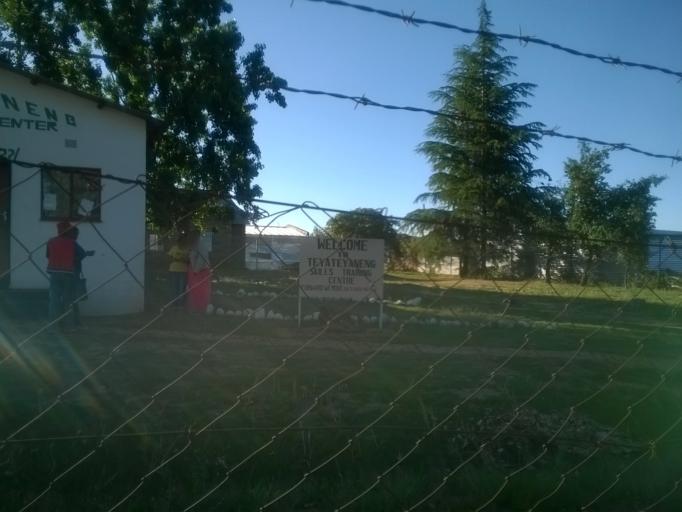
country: LS
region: Berea
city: Teyateyaneng
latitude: -29.1457
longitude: 27.7498
